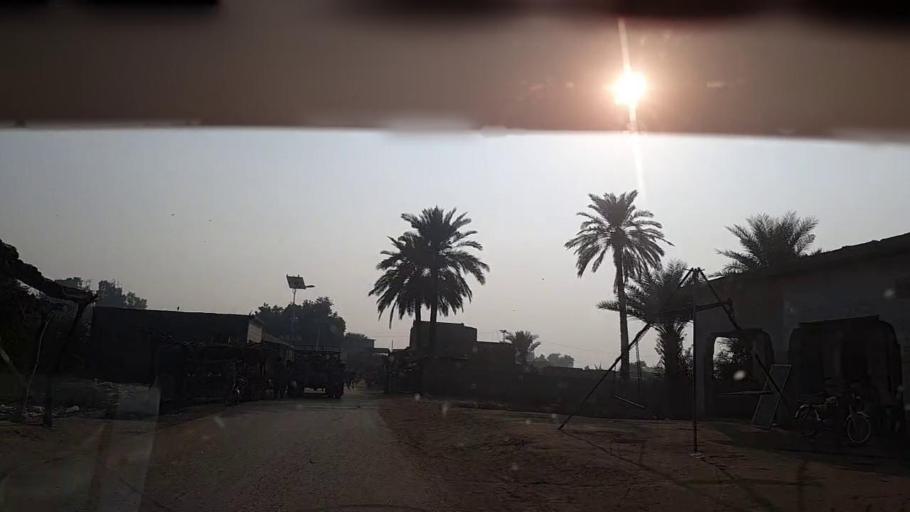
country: PK
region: Sindh
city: Sobhadero
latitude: 27.4427
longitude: 68.3903
